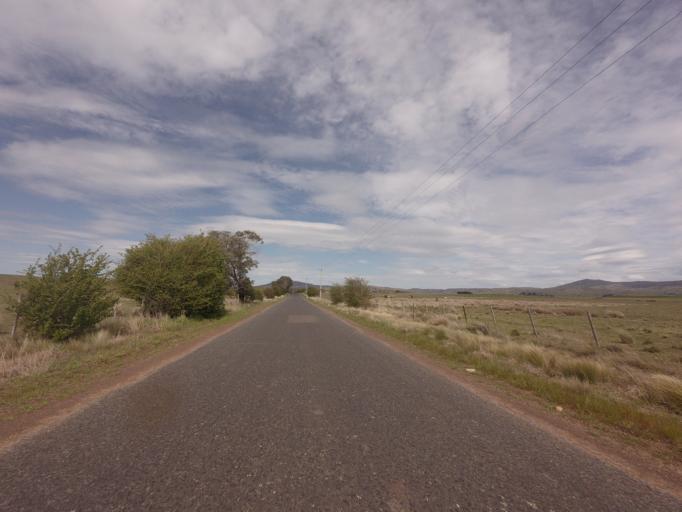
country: AU
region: Tasmania
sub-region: Northern Midlands
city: Evandale
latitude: -41.8711
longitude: 147.3526
